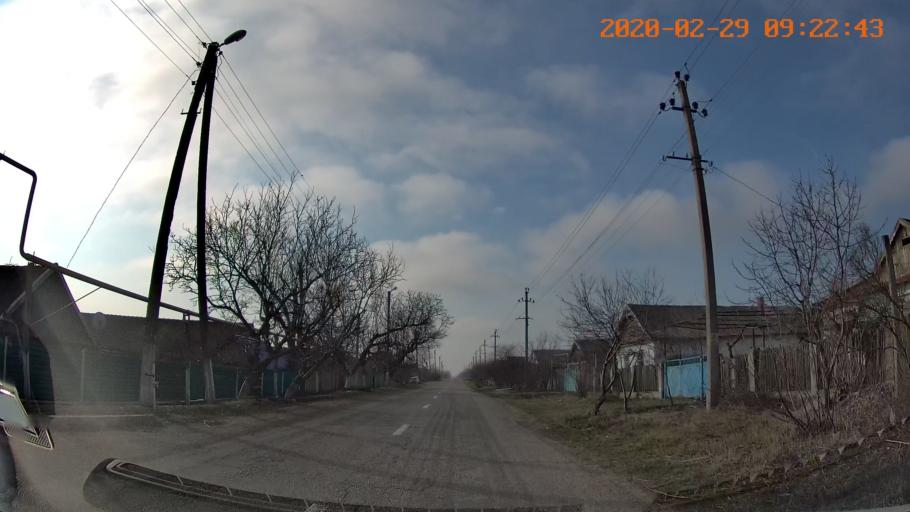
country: MD
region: Telenesti
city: Pervomaisc
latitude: 46.7328
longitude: 29.9633
